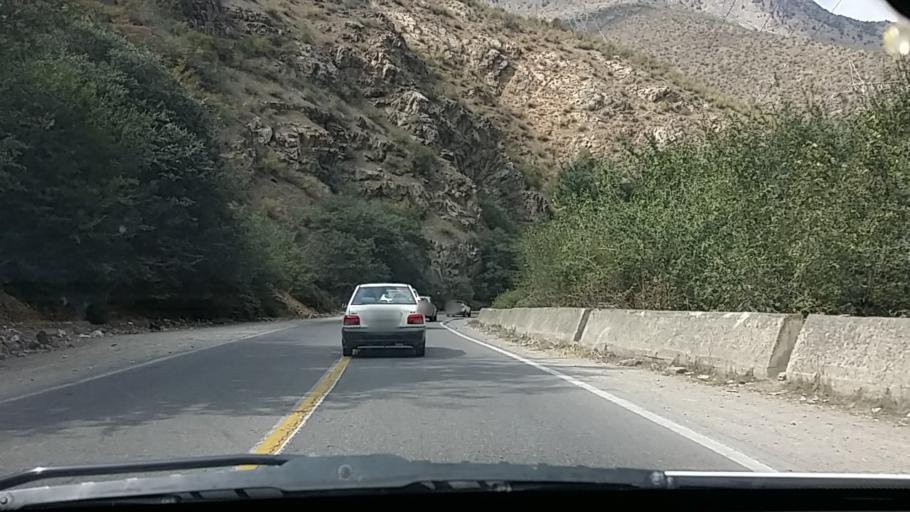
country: IR
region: Mazandaran
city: Chalus
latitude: 36.3454
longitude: 51.2577
